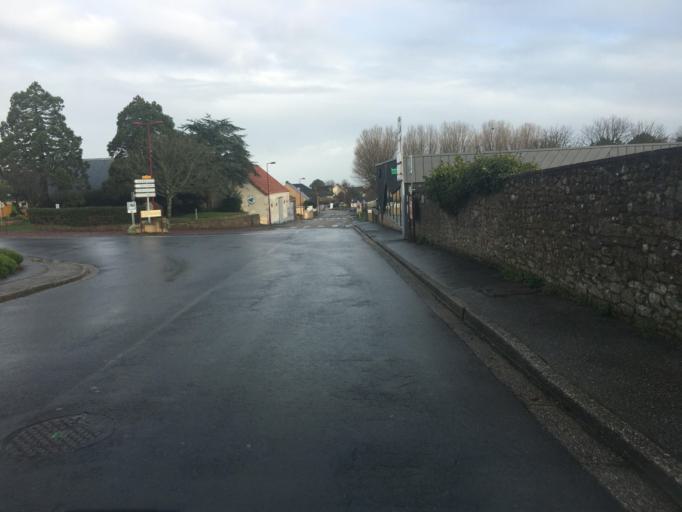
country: FR
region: Lower Normandy
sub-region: Departement de la Manche
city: Saint-Pierre-Eglise
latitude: 49.6679
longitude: -1.4031
